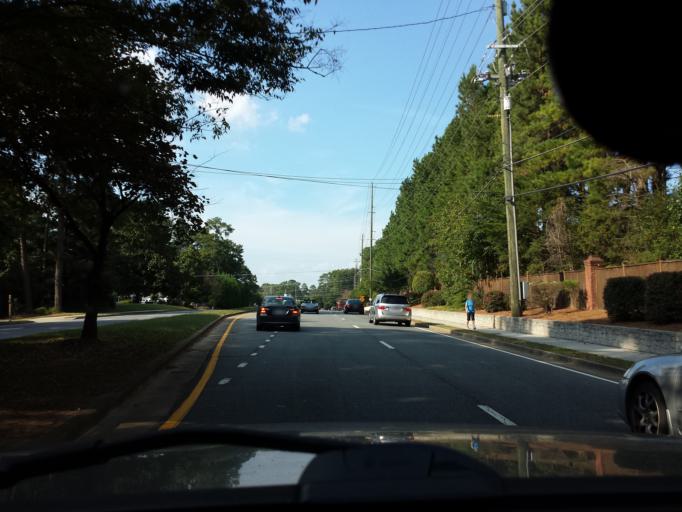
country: US
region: Georgia
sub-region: Cobb County
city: Vinings
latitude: 33.9354
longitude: -84.4609
